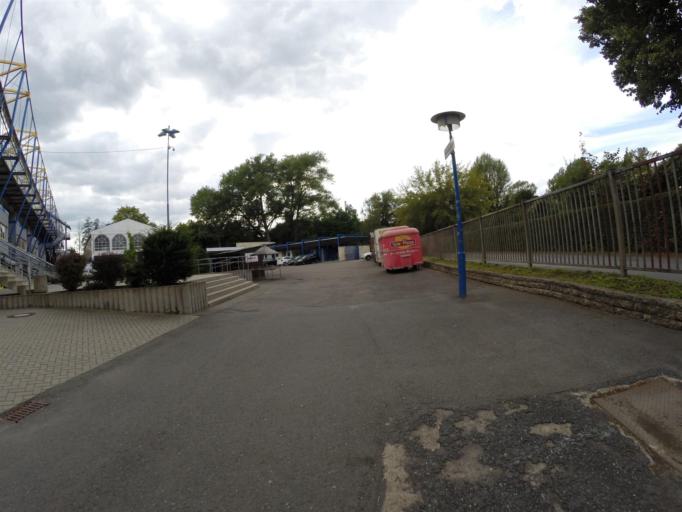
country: DE
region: Thuringia
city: Jena
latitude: 50.9169
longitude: 11.5828
